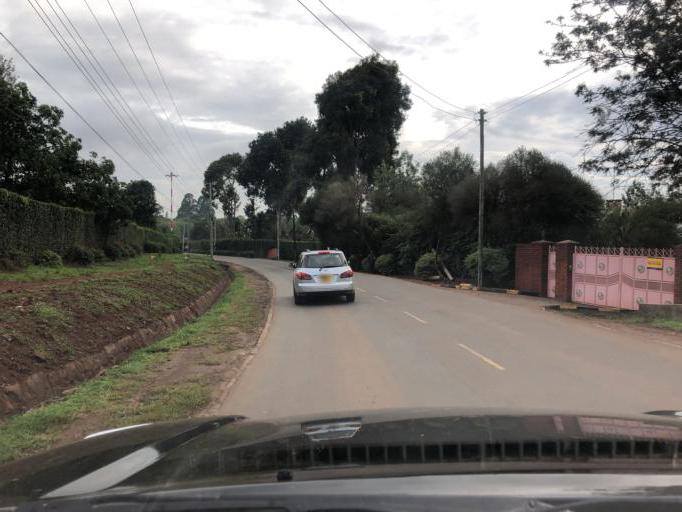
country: KE
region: Kajiado
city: Ngong
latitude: -1.3401
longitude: 36.7143
